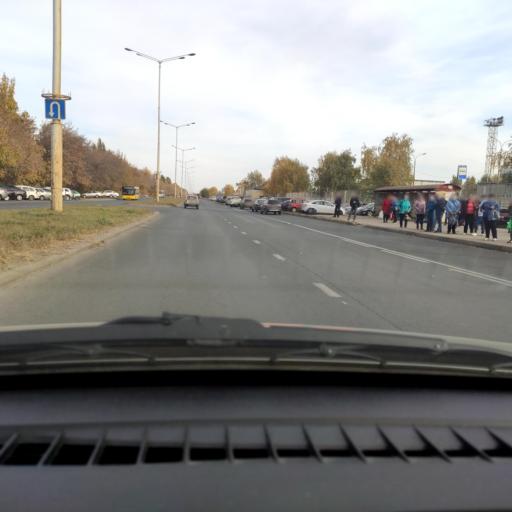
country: RU
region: Samara
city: Tol'yatti
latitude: 53.5696
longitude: 49.2569
